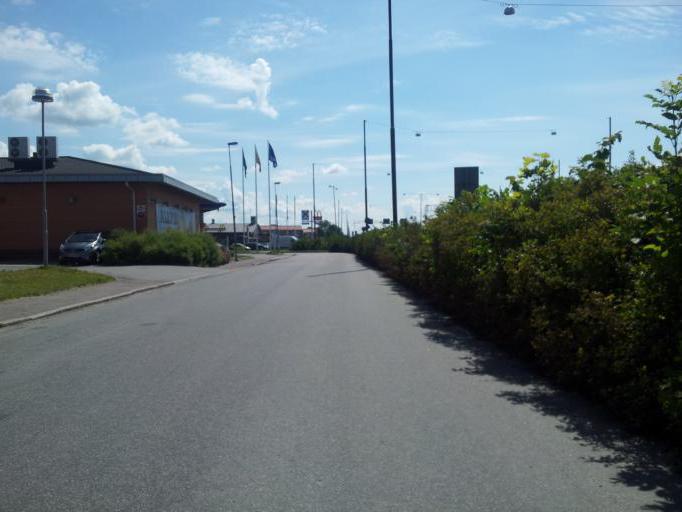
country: SE
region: Uppsala
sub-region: Uppsala Kommun
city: Uppsala
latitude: 59.8690
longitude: 17.6584
